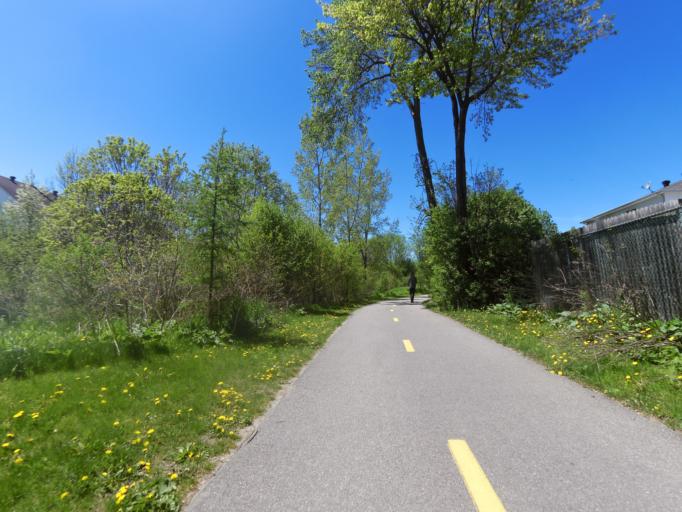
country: CA
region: Ontario
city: Ottawa
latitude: 45.4373
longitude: -75.7770
